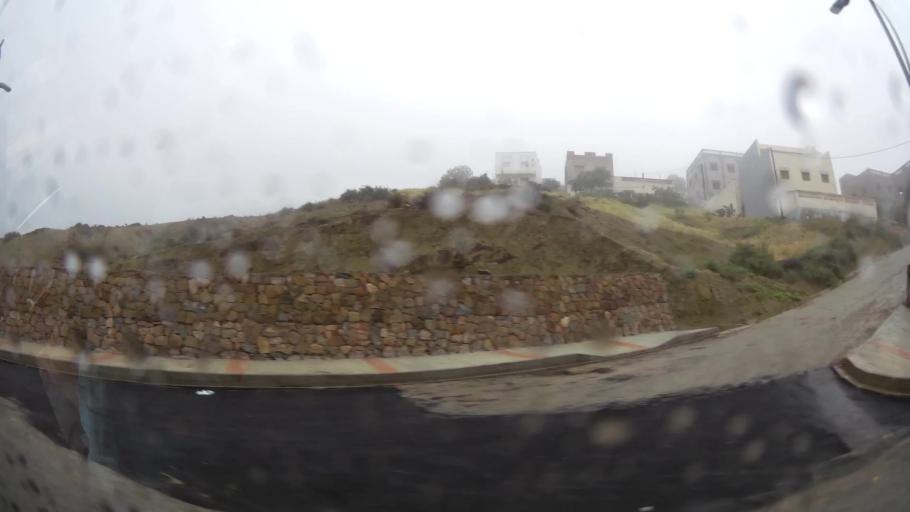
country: MA
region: Taza-Al Hoceima-Taounate
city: Tirhanimine
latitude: 35.2345
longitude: -3.9520
